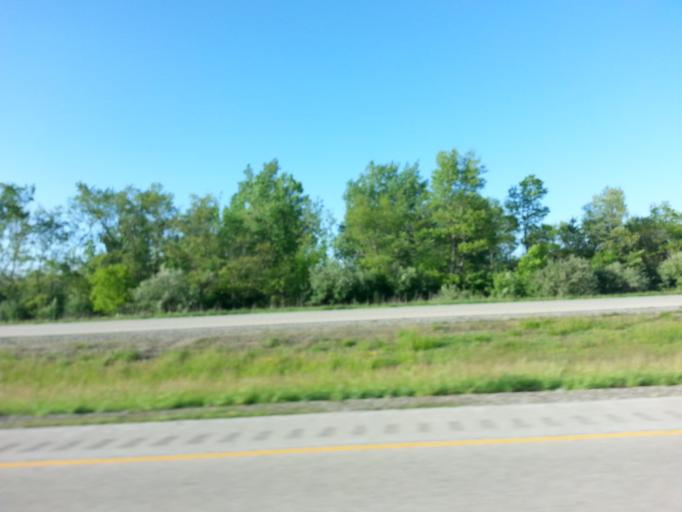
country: US
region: Illinois
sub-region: McLean County
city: Downs
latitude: 40.3947
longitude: -88.8877
